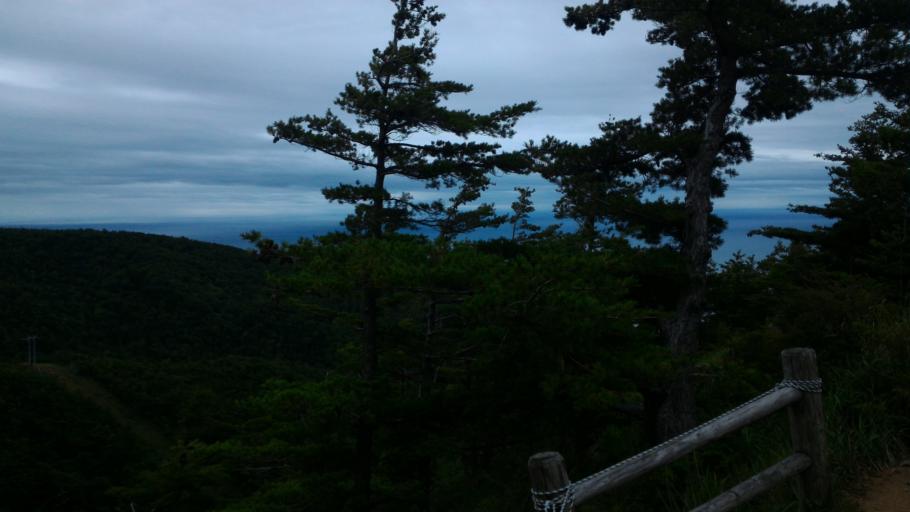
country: JP
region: Hokkaido
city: Shizunai-furukawacho
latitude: 42.1054
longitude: 143.0117
